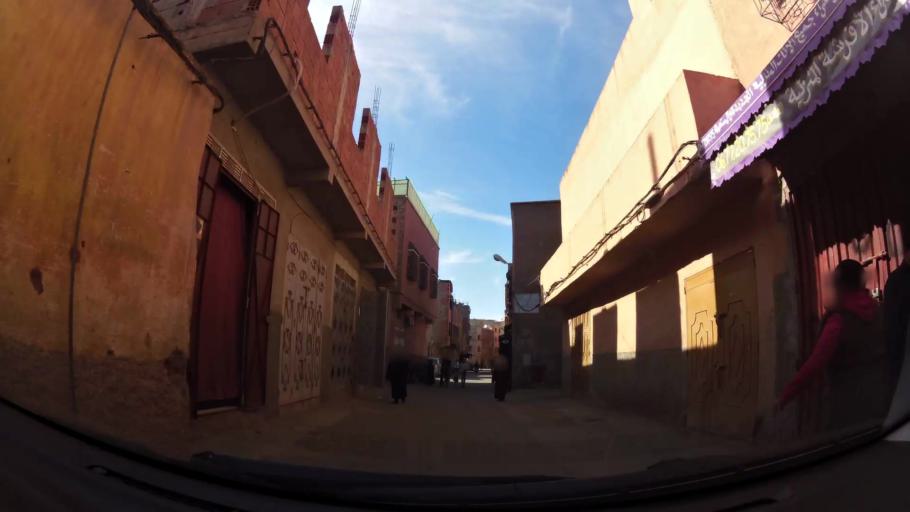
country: MA
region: Marrakech-Tensift-Al Haouz
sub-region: Marrakech
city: Marrakesh
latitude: 31.6143
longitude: -7.9660
